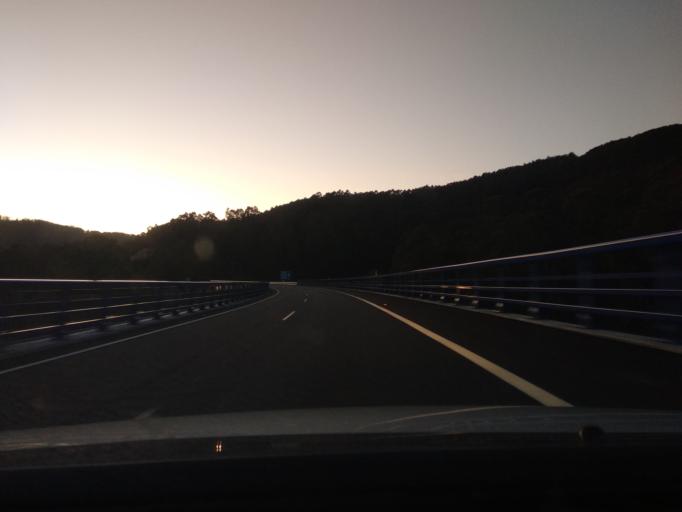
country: ES
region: Galicia
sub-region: Provincia de Pontevedra
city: Moana
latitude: 42.3086
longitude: -8.7235
